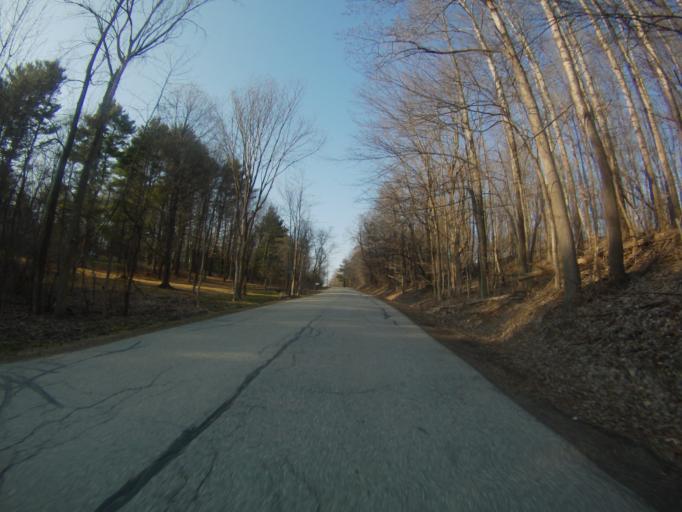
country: US
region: Vermont
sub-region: Addison County
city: Middlebury (village)
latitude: 44.0330
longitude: -73.1450
